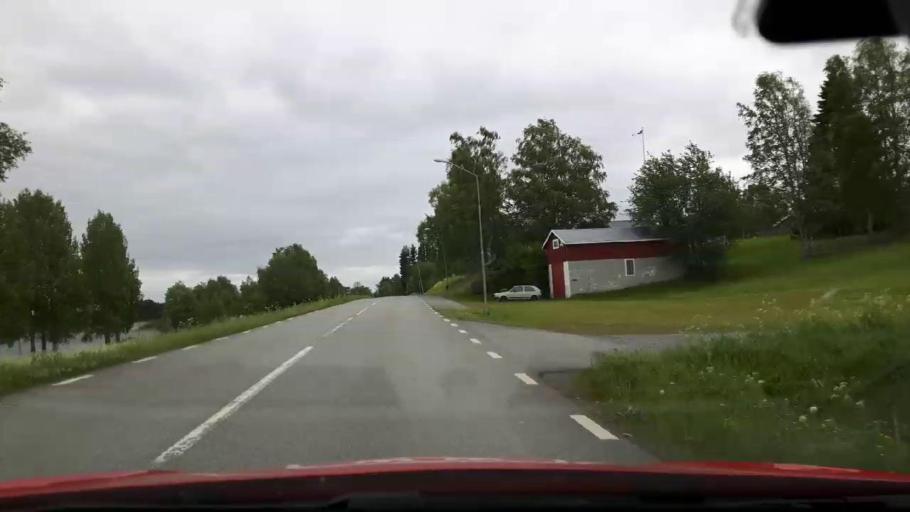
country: SE
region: Jaemtland
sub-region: Stroemsunds Kommun
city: Stroemsund
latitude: 63.5794
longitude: 15.3648
